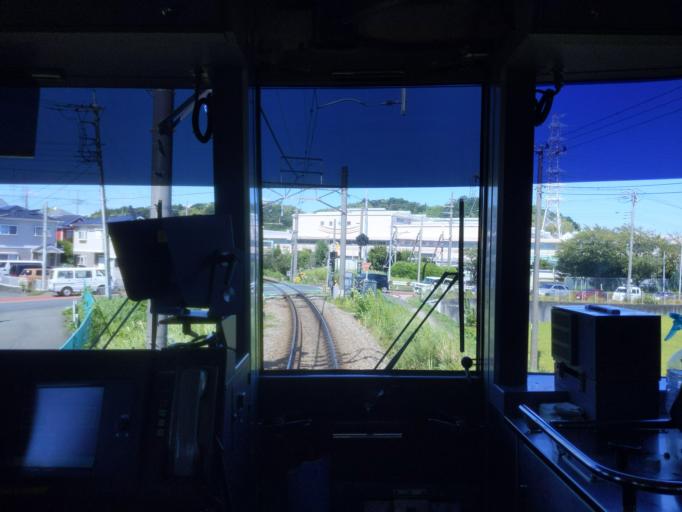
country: JP
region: Tokyo
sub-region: Machida-shi
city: Machida
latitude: 35.5416
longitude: 139.4940
